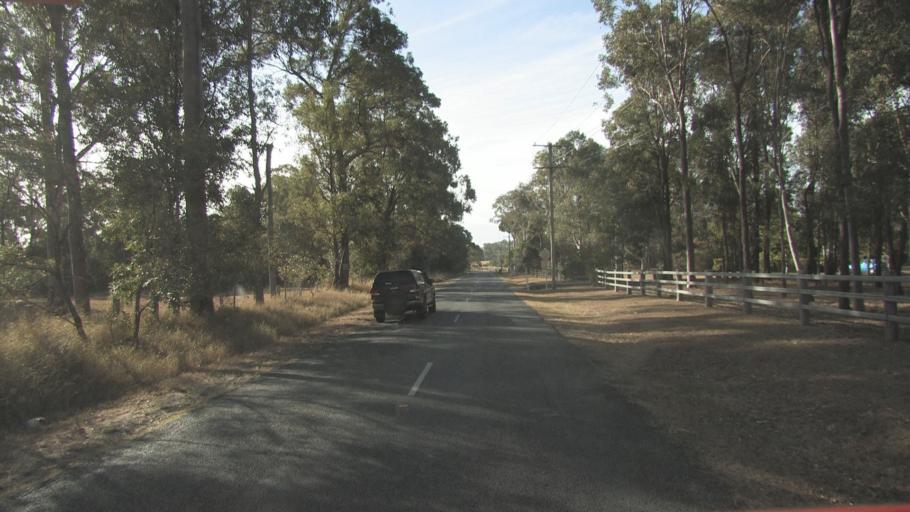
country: AU
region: Queensland
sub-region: Logan
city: Cedar Vale
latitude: -27.8690
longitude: 153.0112
